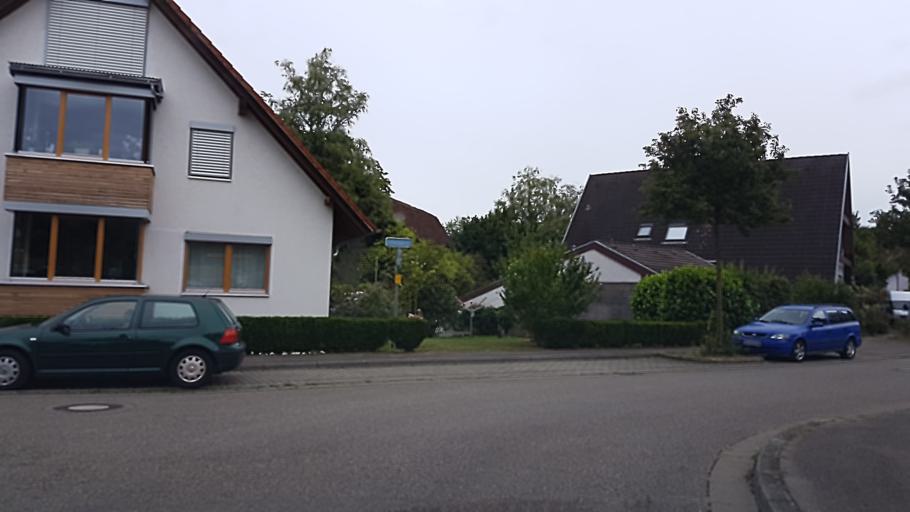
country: DE
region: Baden-Wuerttemberg
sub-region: Freiburg Region
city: Gottenheim
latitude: 48.0139
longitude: 7.7244
